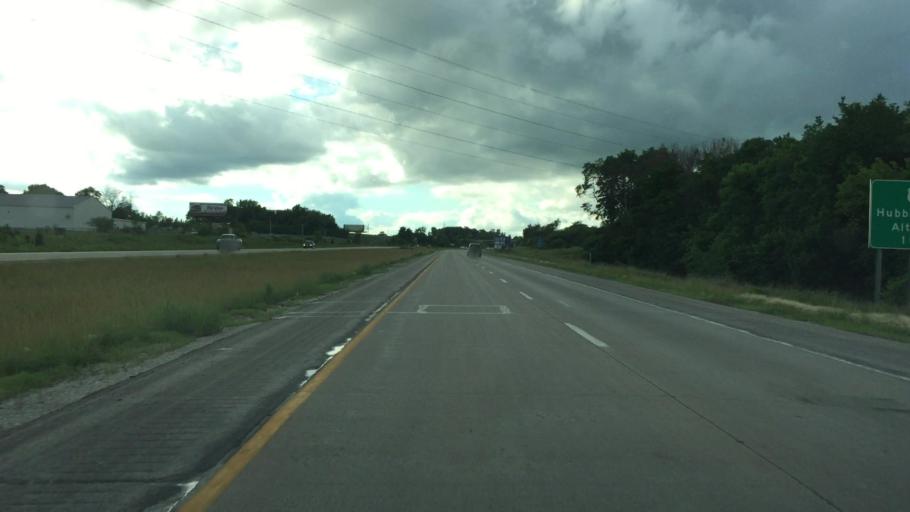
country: US
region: Iowa
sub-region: Polk County
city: Altoona
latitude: 41.6263
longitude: -93.4970
